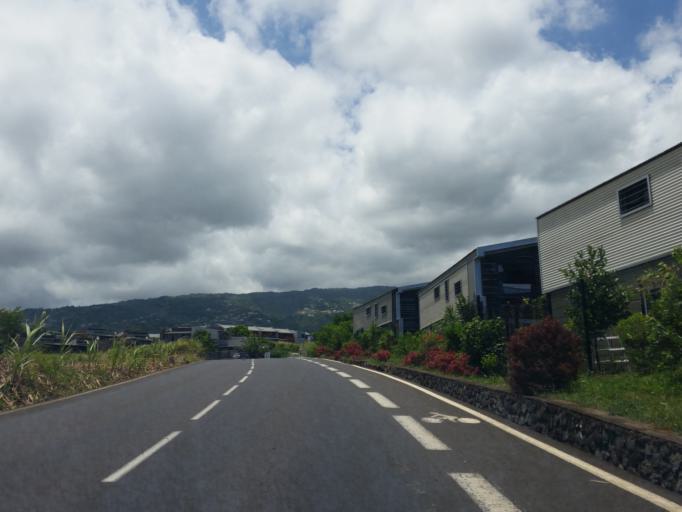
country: RE
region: Reunion
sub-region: Reunion
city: Sainte-Marie
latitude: -20.9132
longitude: 55.5198
